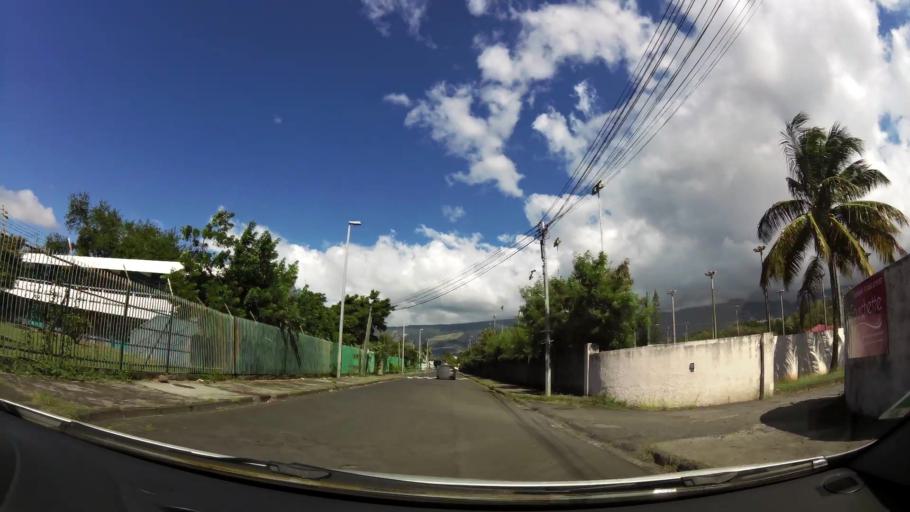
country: RE
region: Reunion
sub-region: Reunion
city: Saint-Denis
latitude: -20.8873
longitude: 55.4957
